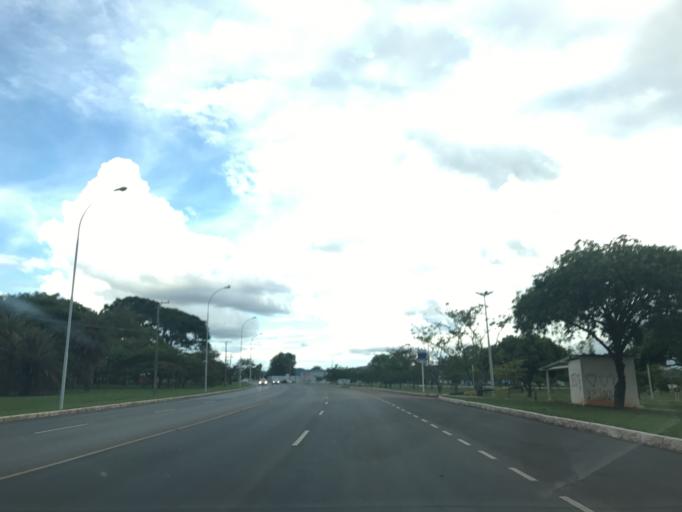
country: BR
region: Federal District
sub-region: Brasilia
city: Brasilia
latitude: -15.7987
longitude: -47.9128
